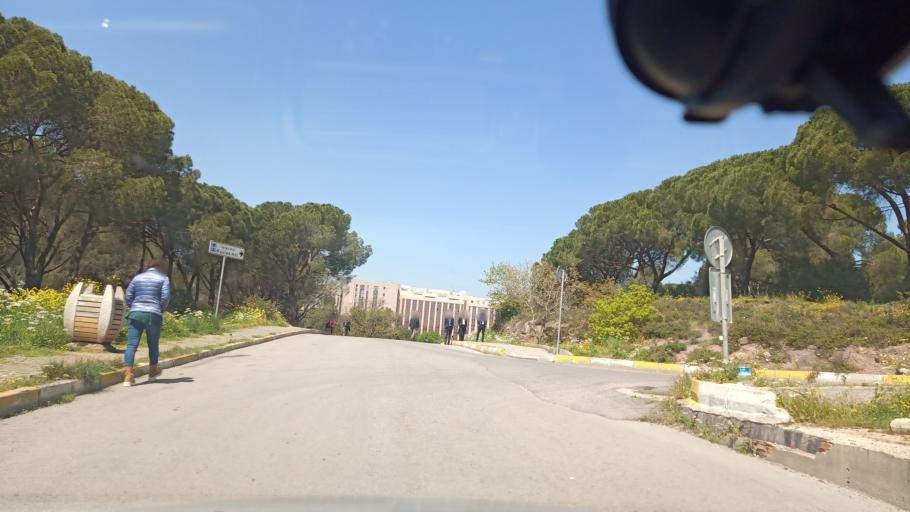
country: TR
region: Istanbul
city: Maltepe
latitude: 40.9477
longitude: 29.1413
